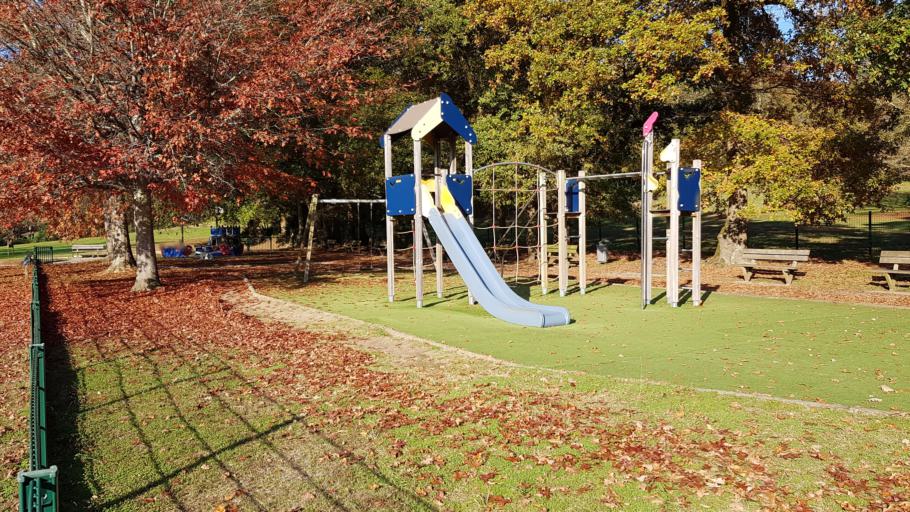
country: FR
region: Aquitaine
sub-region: Departement des Landes
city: Saint-Paul-les-Dax
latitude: 43.7318
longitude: -1.0700
